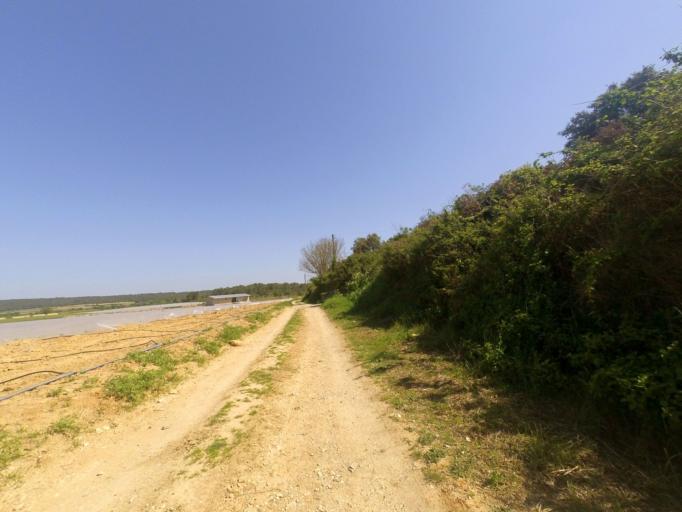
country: FR
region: Languedoc-Roussillon
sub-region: Departement du Gard
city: Calvisson
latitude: 43.7640
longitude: 4.1978
